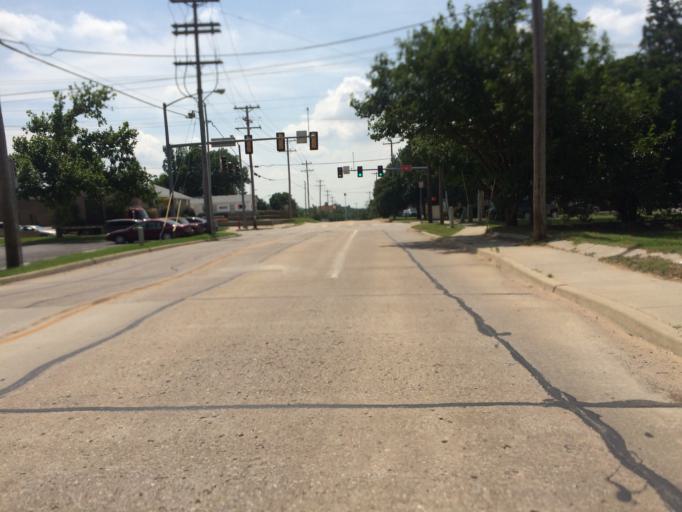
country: US
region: Oklahoma
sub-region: Cleveland County
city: Norman
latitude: 35.2076
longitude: -97.4760
